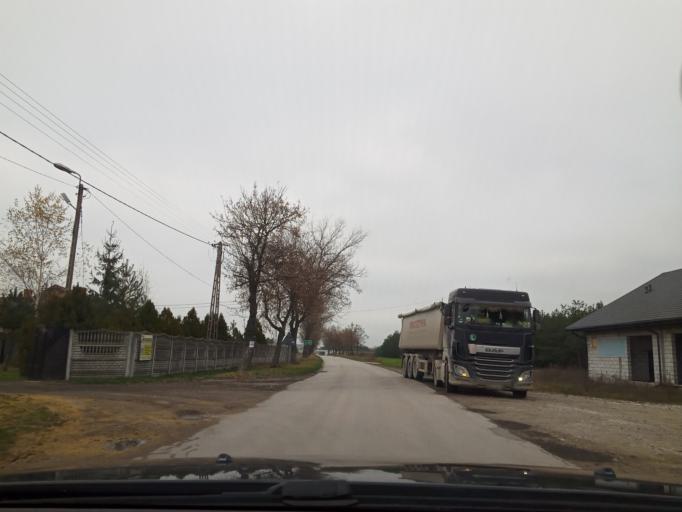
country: PL
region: Swietokrzyskie
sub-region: Powiat jedrzejowski
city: Imielno
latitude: 50.5933
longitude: 20.4800
